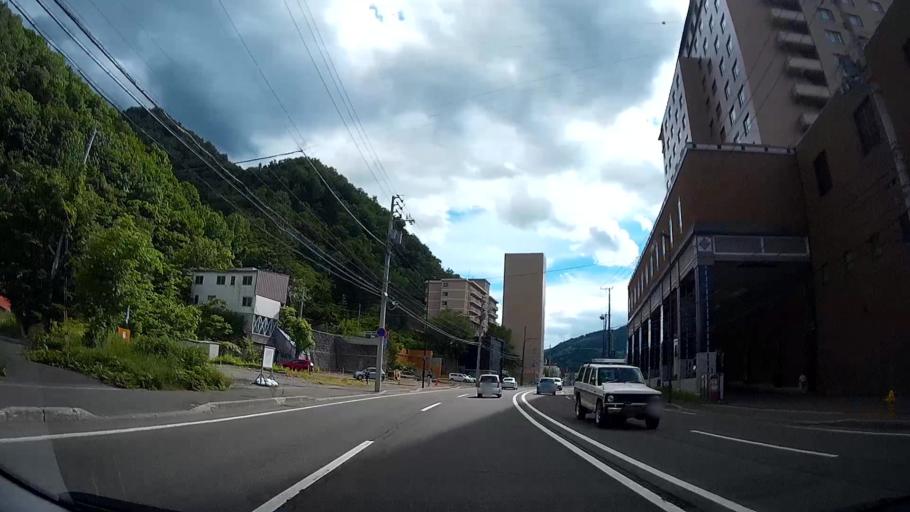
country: JP
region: Hokkaido
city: Sapporo
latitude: 42.9643
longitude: 141.1644
